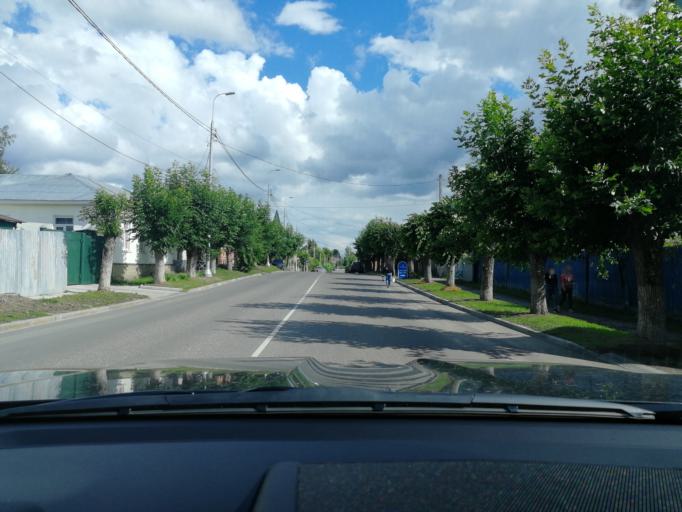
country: RU
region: Moskovskaya
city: Serpukhov
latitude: 54.9154
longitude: 37.4219
